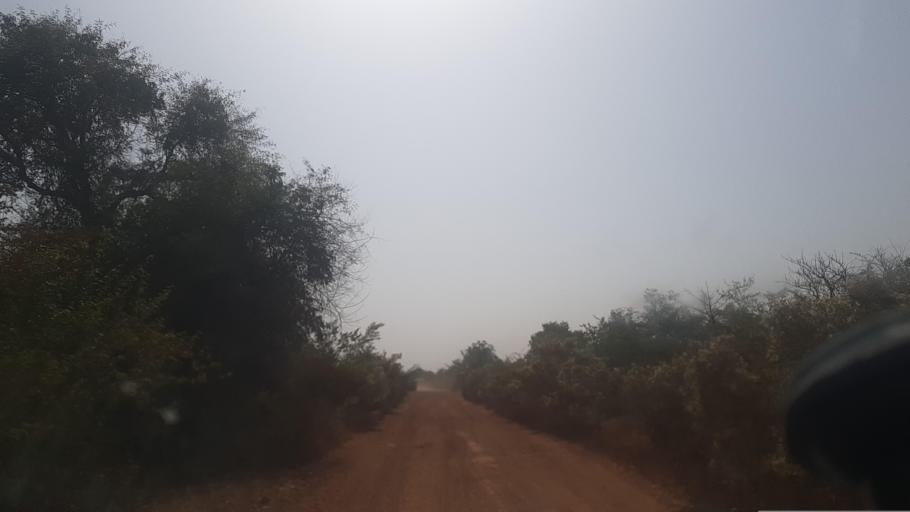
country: ML
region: Segou
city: Baroueli
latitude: 13.0768
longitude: -6.4838
